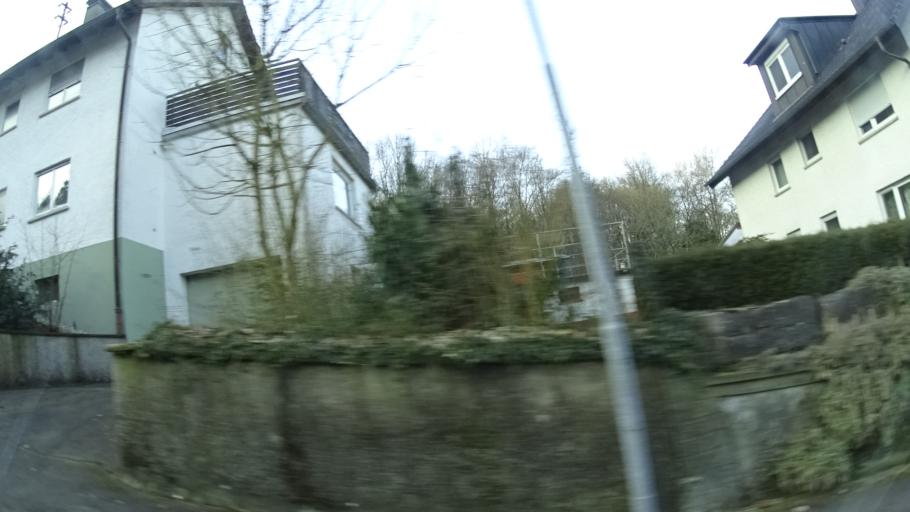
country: DE
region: Baden-Wuerttemberg
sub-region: Karlsruhe Region
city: Mosbach
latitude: 49.3433
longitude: 9.1372
